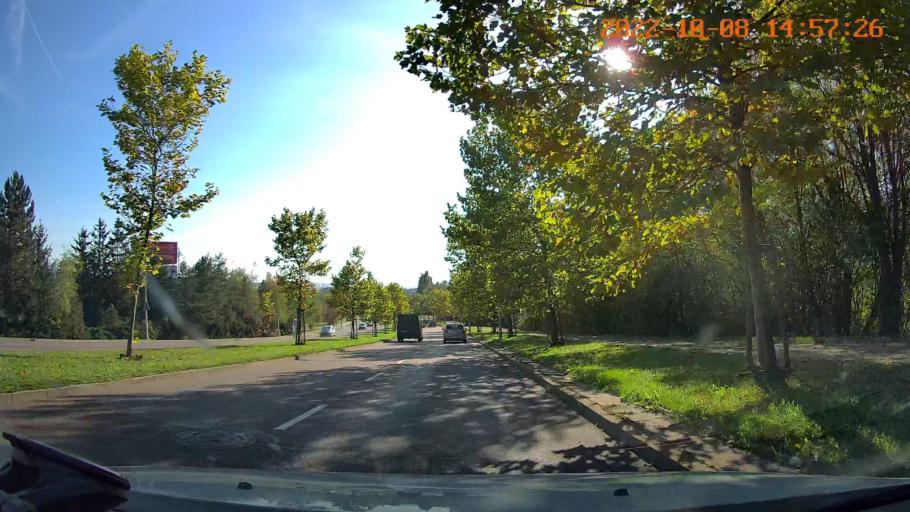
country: PL
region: Lesser Poland Voivodeship
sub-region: Powiat tarnowski
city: Tarnow
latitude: 50.0313
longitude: 20.9994
